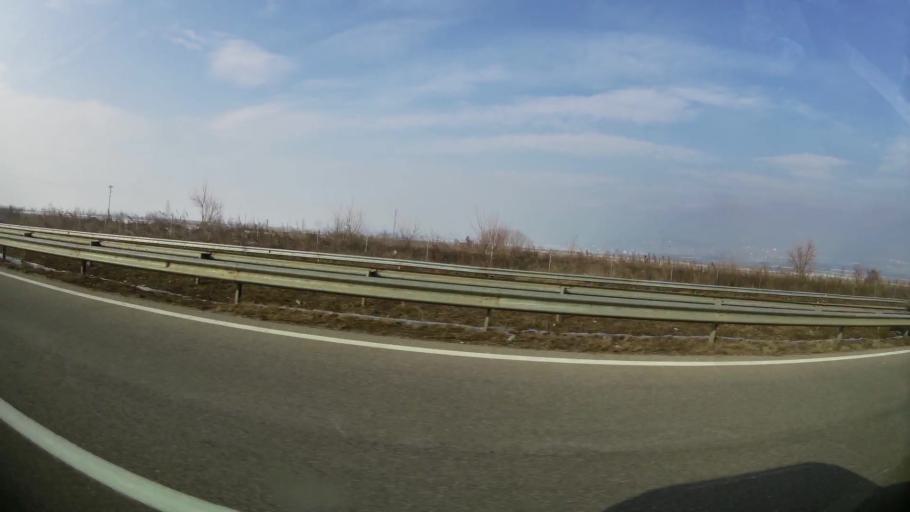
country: MK
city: Creshevo
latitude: 42.0333
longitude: 21.5159
